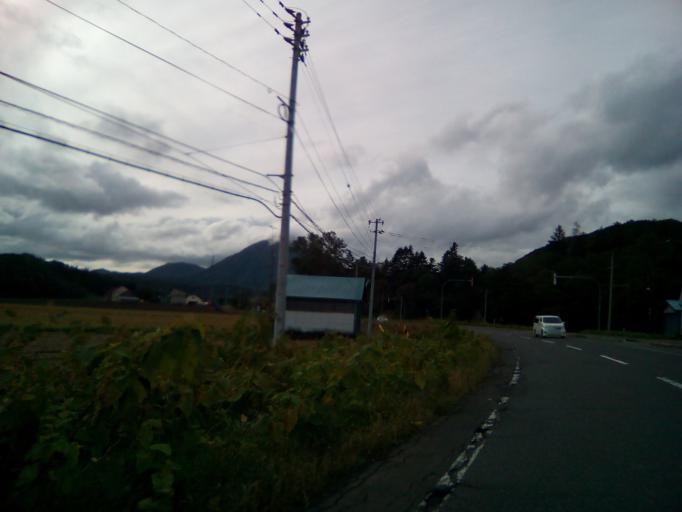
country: JP
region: Hokkaido
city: Niseko Town
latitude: 42.7675
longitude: 140.9862
